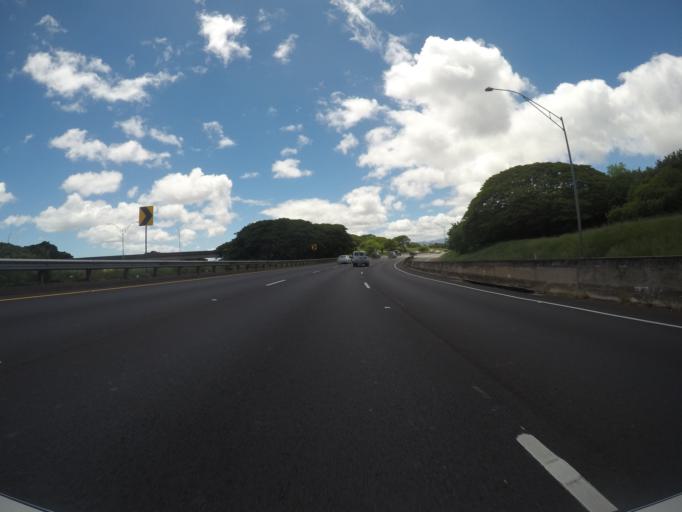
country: US
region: Hawaii
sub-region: Honolulu County
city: Halawa
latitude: 21.3725
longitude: -157.9215
